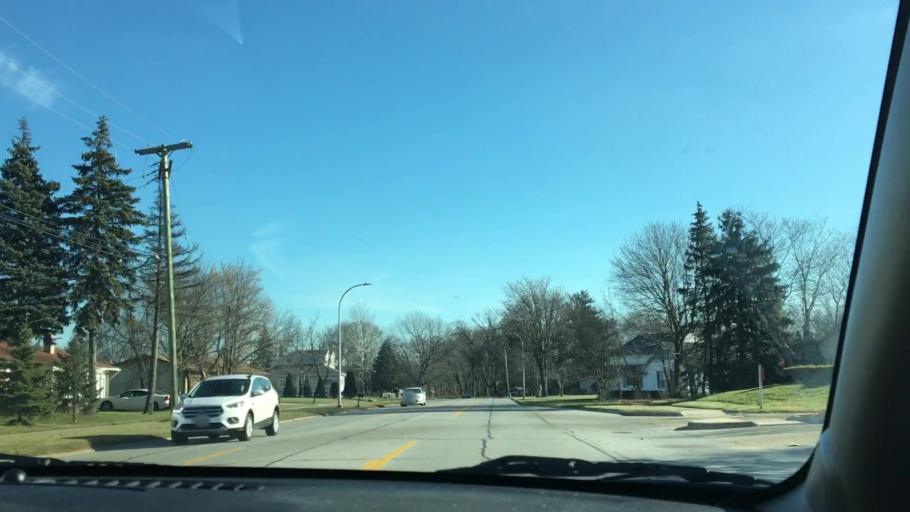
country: US
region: Michigan
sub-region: Wayne County
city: Livonia
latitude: 42.3478
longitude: -83.3665
